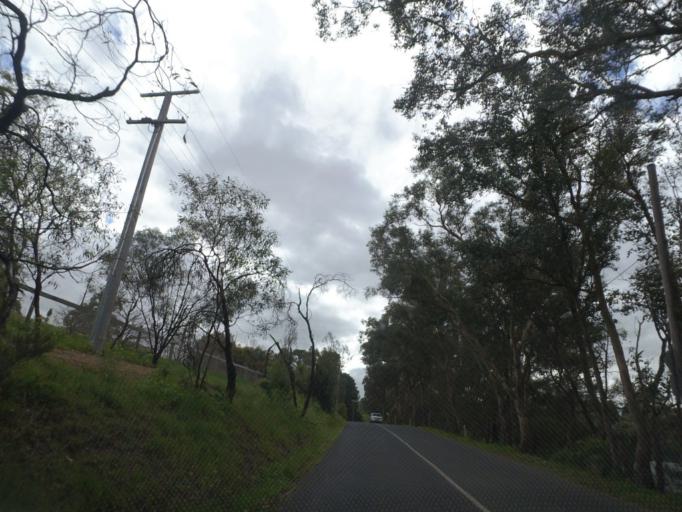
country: AU
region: Victoria
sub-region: Nillumbik
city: Diamond Creek
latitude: -37.6542
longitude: 145.1582
